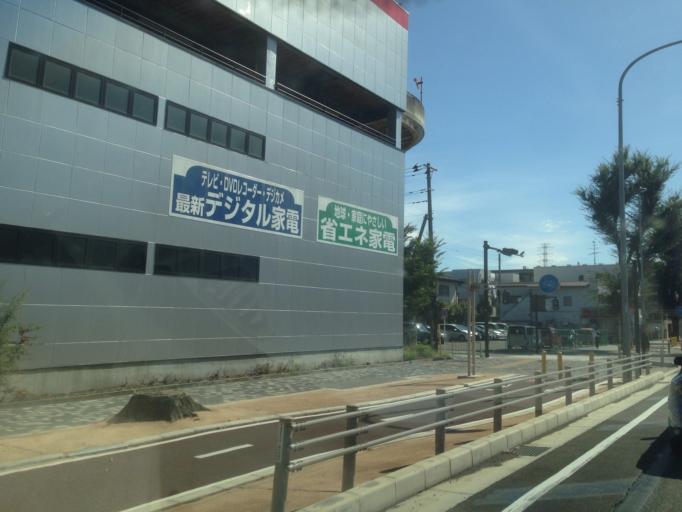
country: JP
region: Tokyo
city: Hachioji
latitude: 35.5777
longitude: 139.3640
